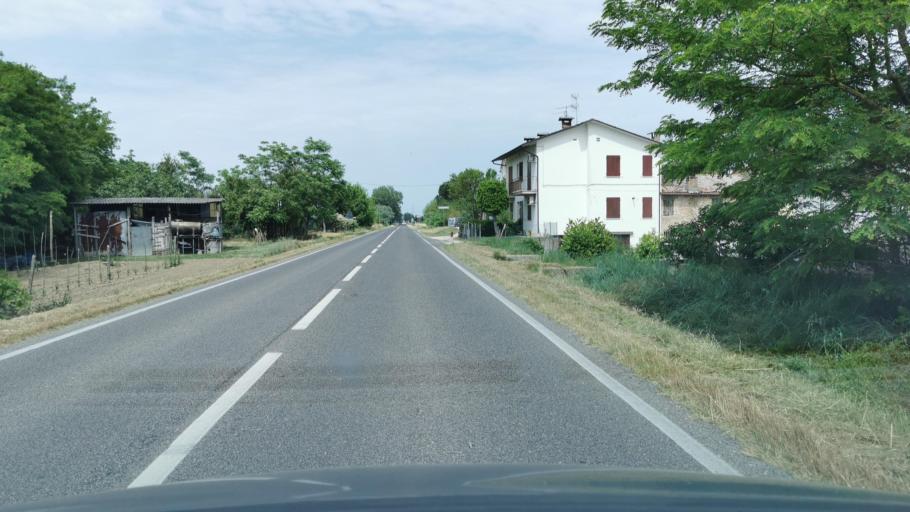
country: IT
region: Emilia-Romagna
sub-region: Provincia di Ravenna
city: Savarna-Conventella
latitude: 44.5153
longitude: 12.1033
